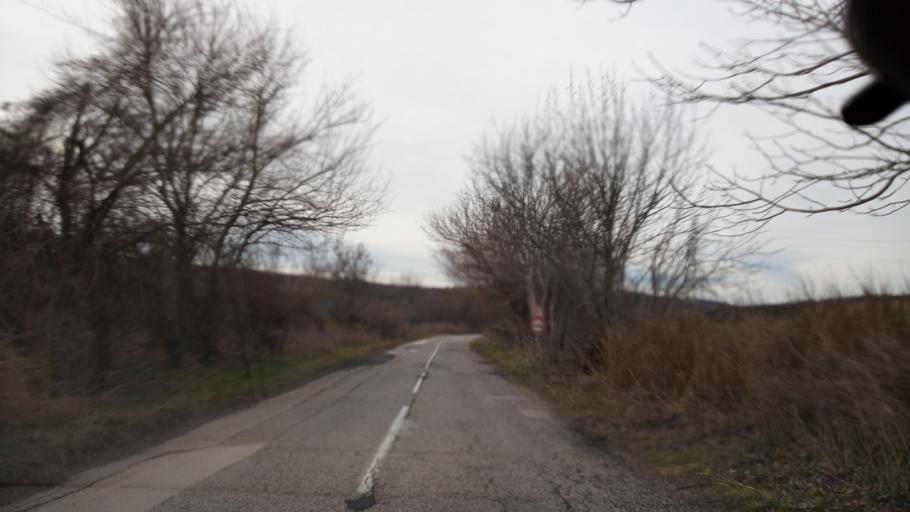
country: BG
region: Pleven
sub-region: Obshtina Belene
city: Belene
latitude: 43.6214
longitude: 25.0360
